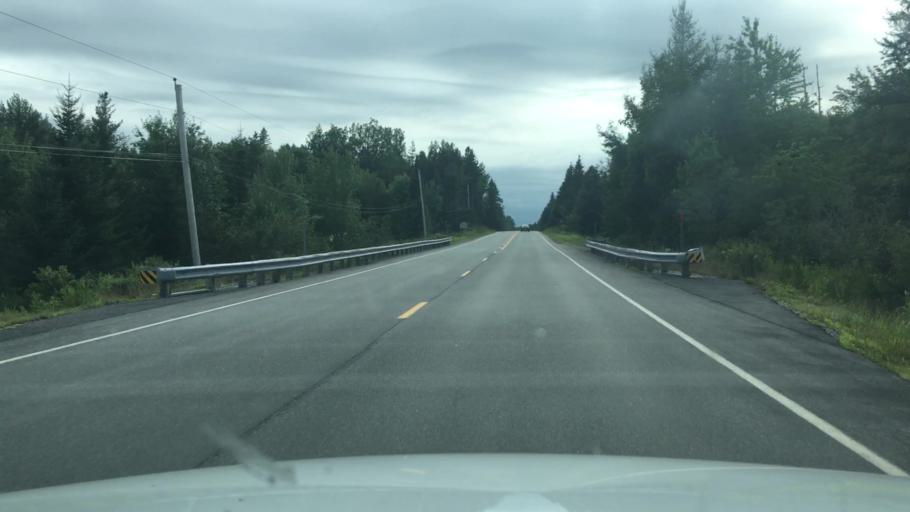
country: US
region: Maine
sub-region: Washington County
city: Cherryfield
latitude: 44.6157
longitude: -67.8542
